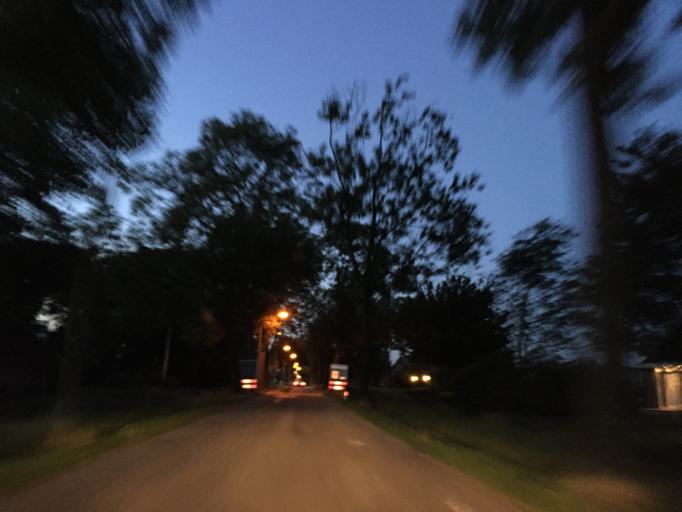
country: NL
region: South Holland
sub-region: Gemeente Waddinxveen
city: Groenswaard
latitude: 52.0391
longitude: 4.6315
